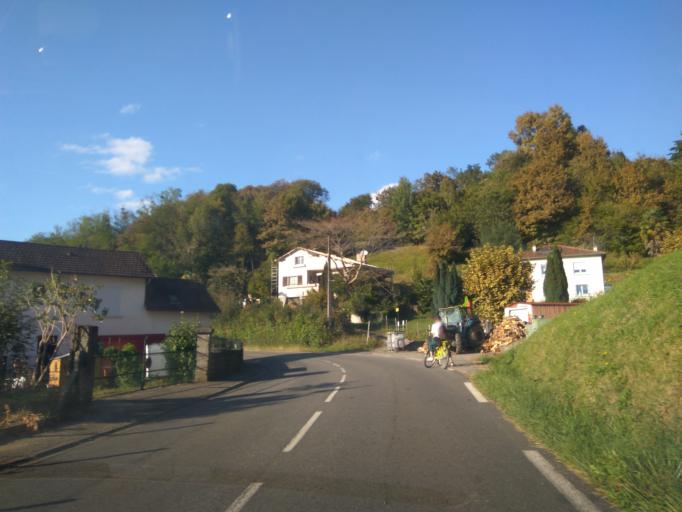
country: FR
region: Aquitaine
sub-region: Departement des Pyrenees-Atlantiques
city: Gelos
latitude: 43.2733
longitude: -0.3708
